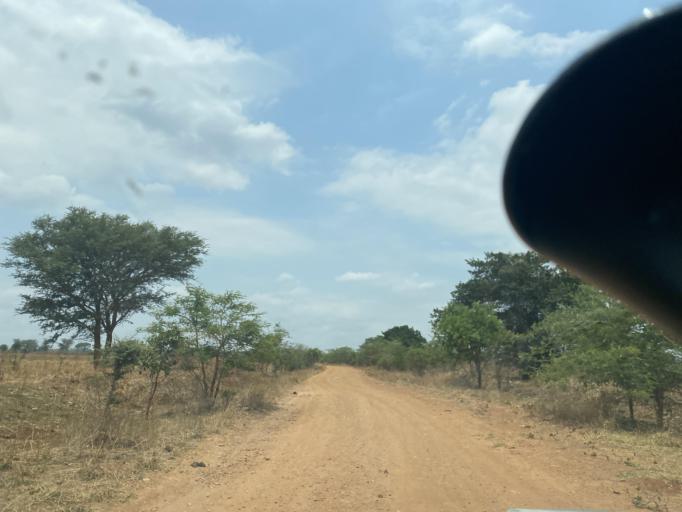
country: ZM
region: Lusaka
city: Chongwe
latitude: -15.5248
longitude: 28.8232
